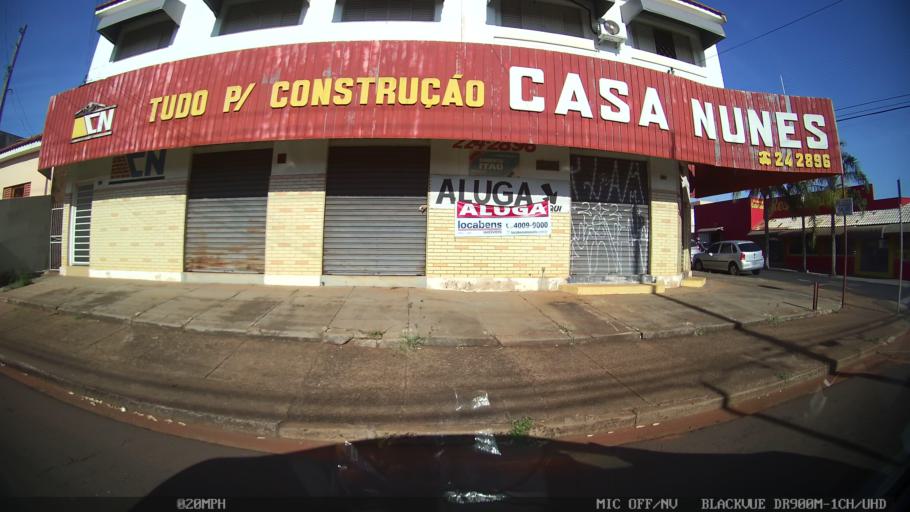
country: BR
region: Sao Paulo
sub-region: Sao Jose Do Rio Preto
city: Sao Jose do Rio Preto
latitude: -20.7988
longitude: -49.3688
